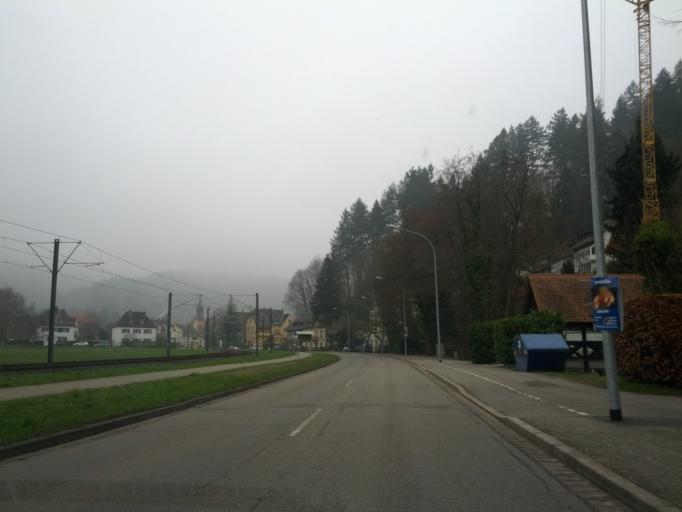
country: DE
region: Baden-Wuerttemberg
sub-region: Freiburg Region
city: Merzhausen
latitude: 47.9681
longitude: 7.8503
